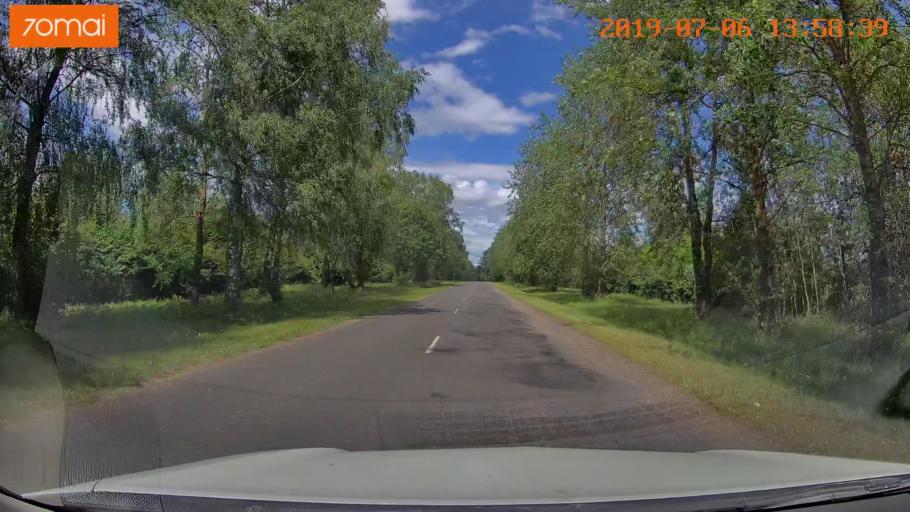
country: BY
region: Minsk
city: Ivyanyets
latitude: 53.7864
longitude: 26.8097
